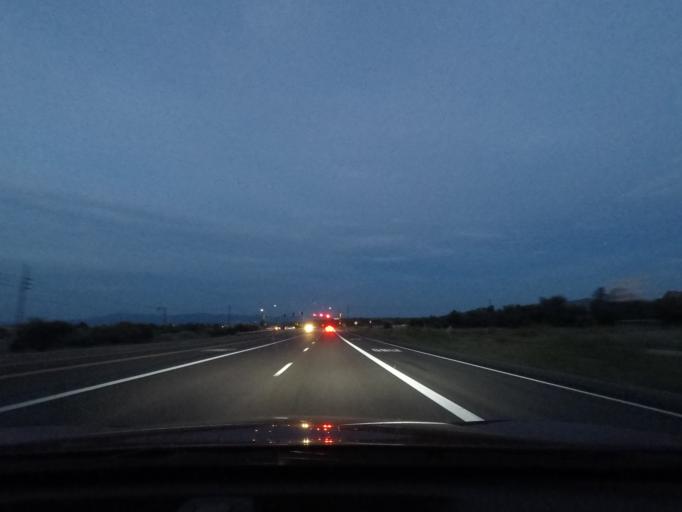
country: US
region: Arizona
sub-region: Yavapai County
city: Prescott
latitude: 34.6291
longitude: -112.4411
